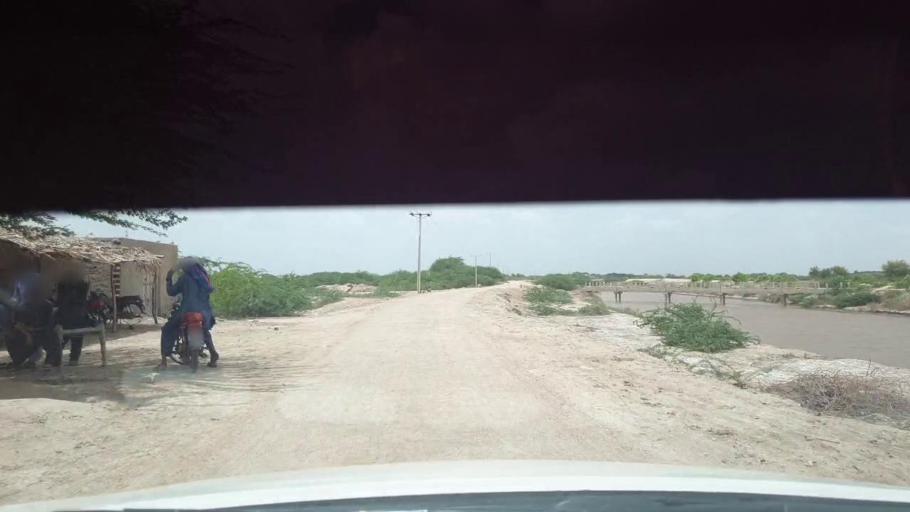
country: PK
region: Sindh
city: Kadhan
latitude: 24.5251
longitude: 69.1232
